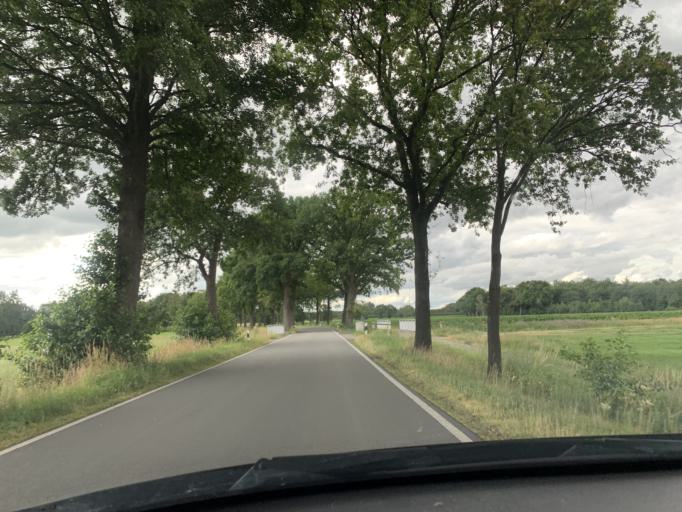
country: DE
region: Lower Saxony
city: Westerstede
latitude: 53.2268
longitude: 7.8880
